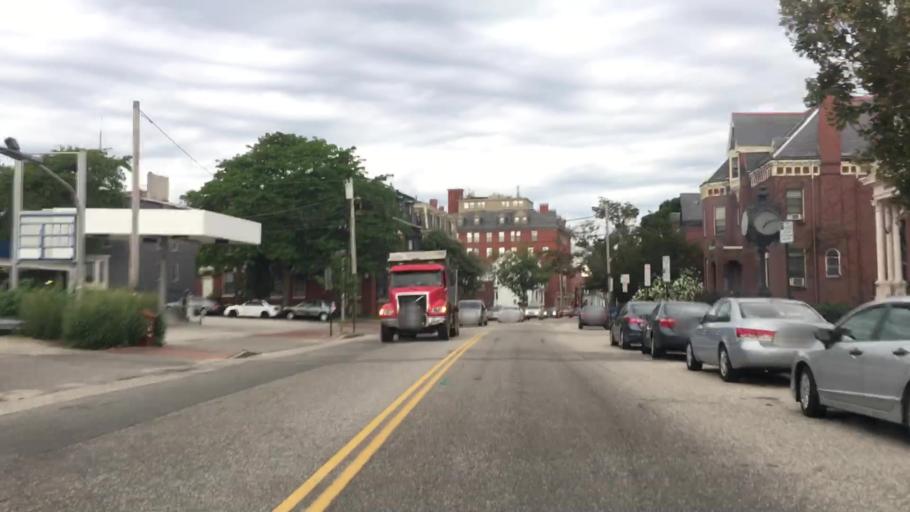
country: US
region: Maine
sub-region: Cumberland County
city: Portland
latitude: 43.6533
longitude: -70.2704
